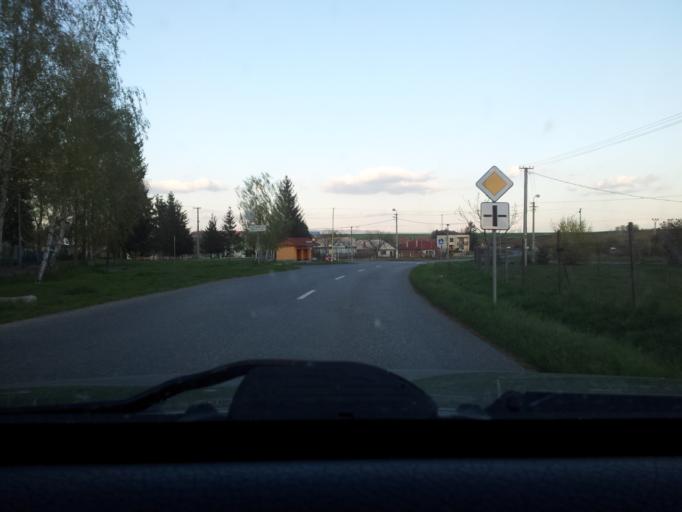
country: SK
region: Nitriansky
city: Tlmace
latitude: 48.2864
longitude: 18.5965
